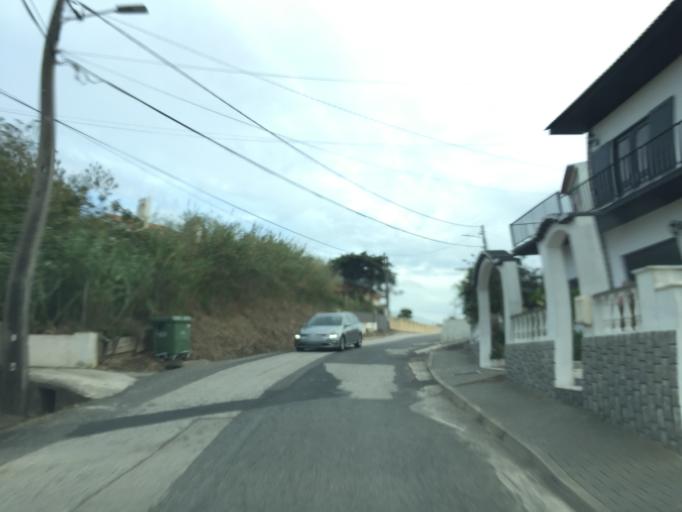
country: PT
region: Leiria
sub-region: Peniche
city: Atouguia da Baleia
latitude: 39.3375
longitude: -9.2987
